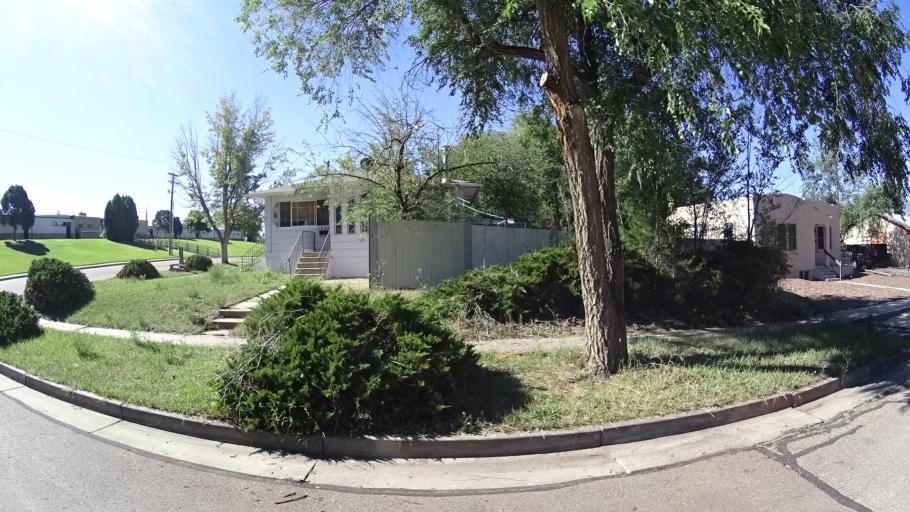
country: US
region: Colorado
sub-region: El Paso County
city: Colorado Springs
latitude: 38.8584
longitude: -104.7828
